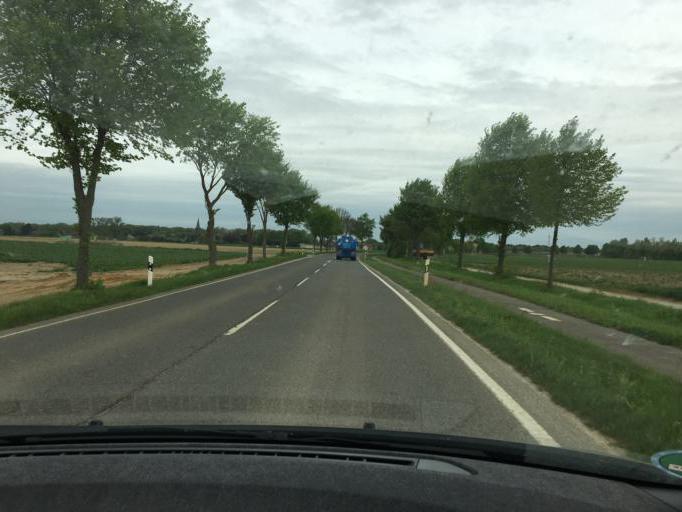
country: DE
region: North Rhine-Westphalia
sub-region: Regierungsbezirk Koln
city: Titz
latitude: 51.0775
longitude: 6.4237
